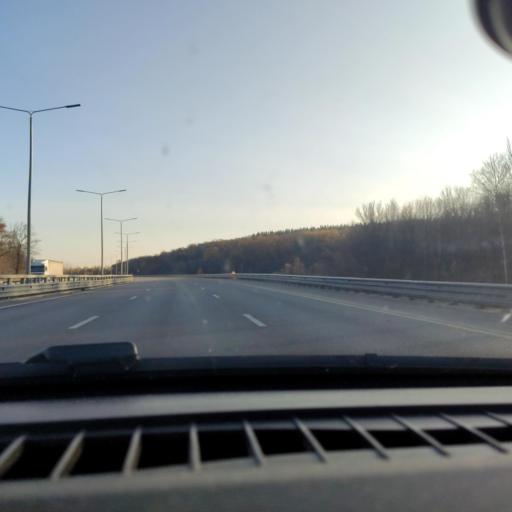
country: RU
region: Voronezj
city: Podgornoye
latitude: 51.8021
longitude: 39.2543
